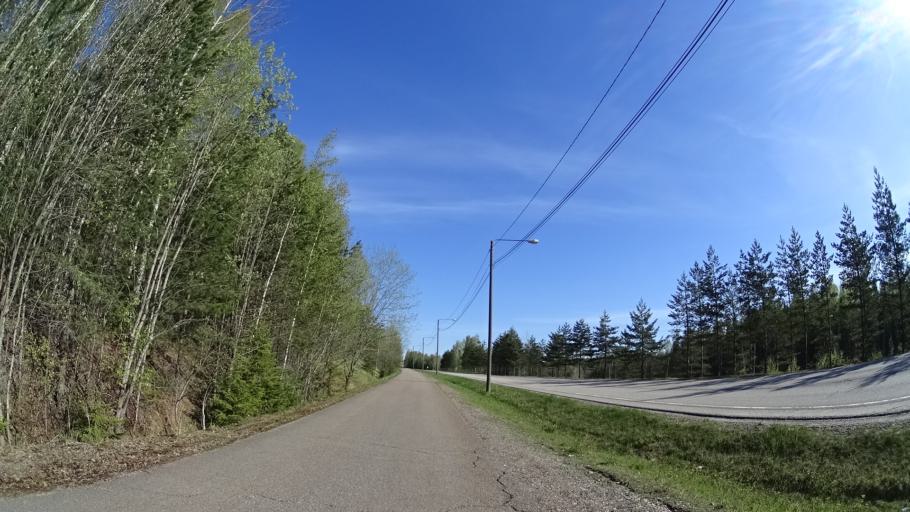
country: FI
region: Uusimaa
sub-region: Helsinki
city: Nurmijaervi
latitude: 60.3584
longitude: 24.8071
